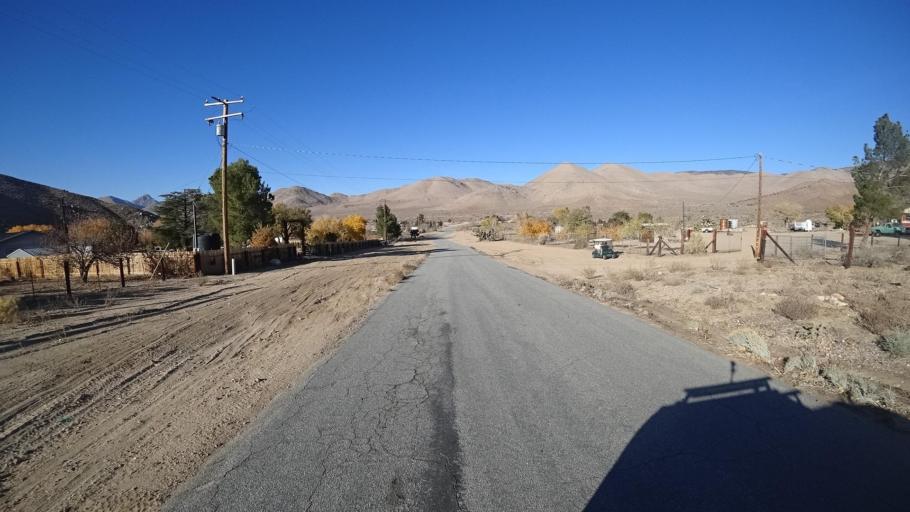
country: US
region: California
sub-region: Kern County
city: Weldon
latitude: 35.5428
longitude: -118.2070
